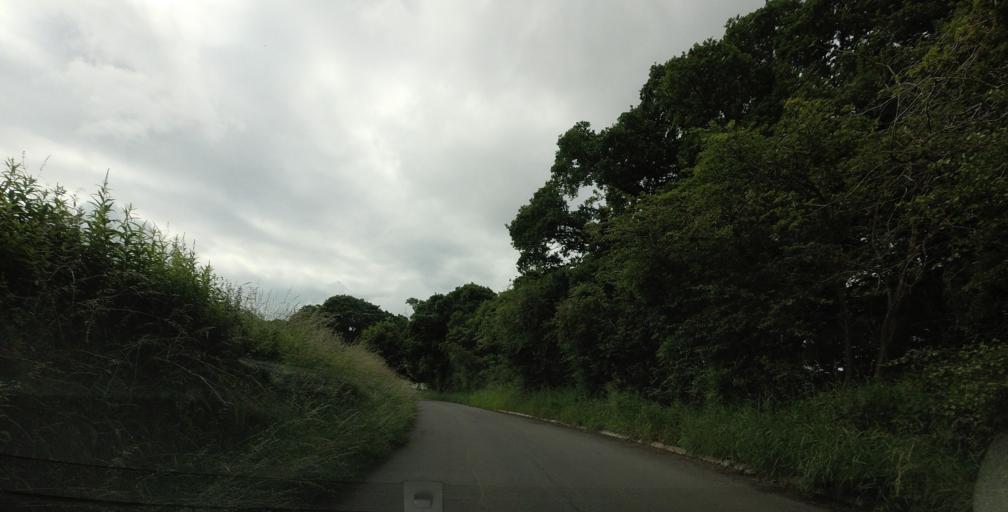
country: GB
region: Scotland
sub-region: West Lothian
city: Kirknewton
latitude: 55.8907
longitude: -3.4049
